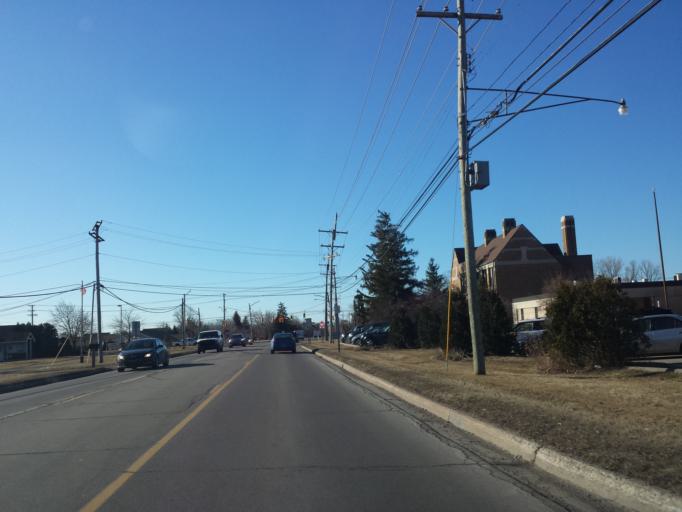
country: US
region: Michigan
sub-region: Oakland County
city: Troy
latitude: 42.6238
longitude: -83.1507
